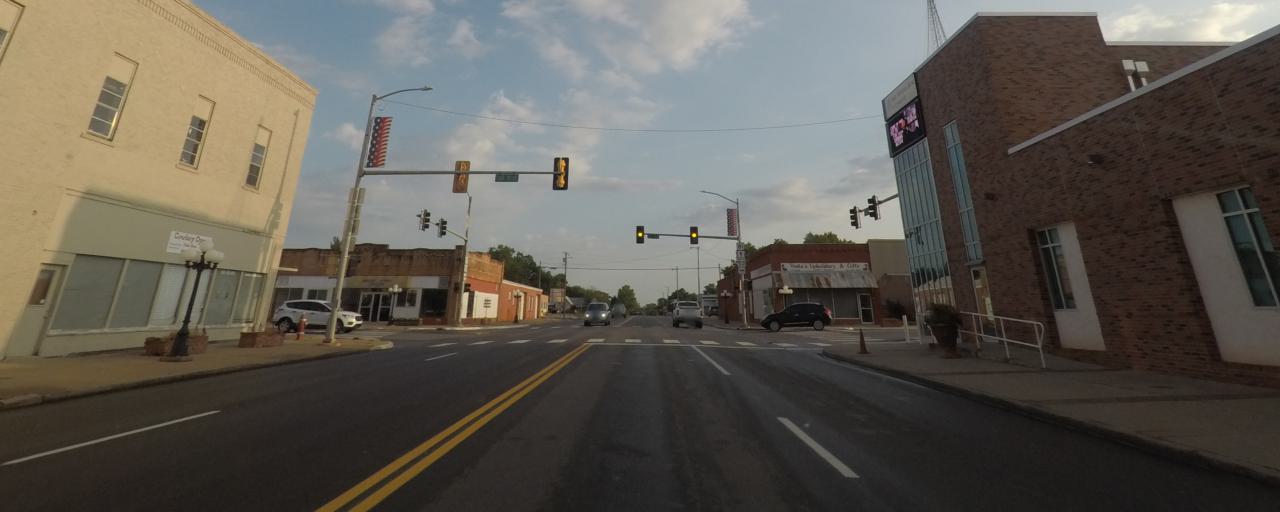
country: US
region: Oklahoma
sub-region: Stephens County
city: Comanche
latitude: 34.3686
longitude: -97.9642
